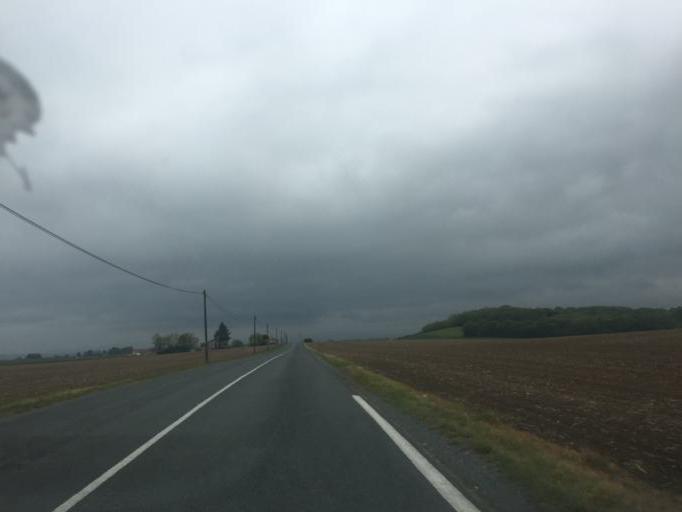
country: FR
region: Rhone-Alpes
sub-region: Departement de l'Ain
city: Civrieux
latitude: 45.9330
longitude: 4.8934
